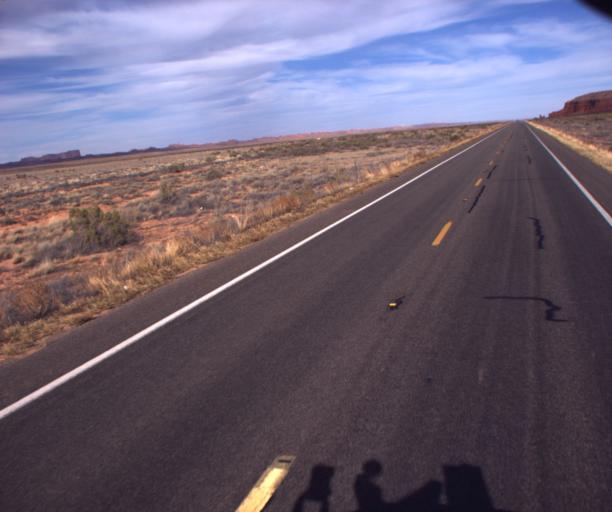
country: US
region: Arizona
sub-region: Navajo County
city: Kayenta
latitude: 36.7598
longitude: -110.0453
